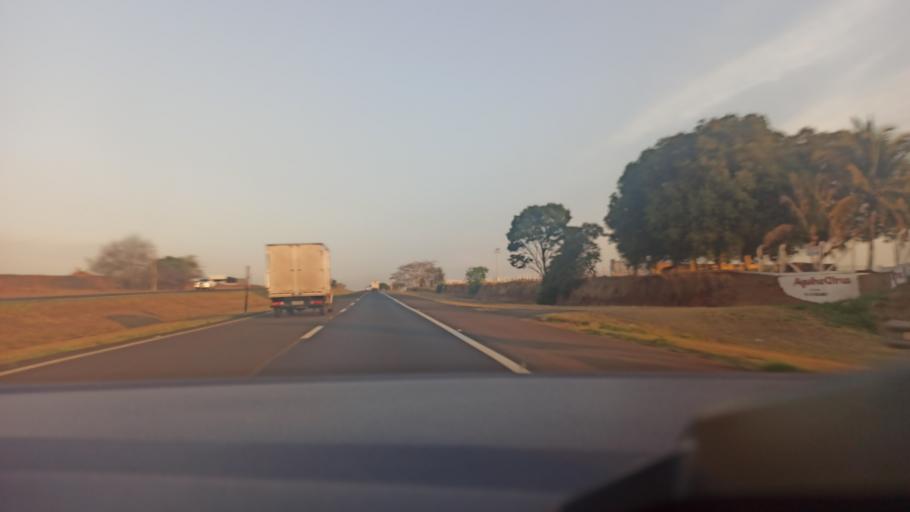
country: BR
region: Sao Paulo
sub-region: Santa Adelia
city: Santa Adelia
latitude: -21.3741
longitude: -48.7452
